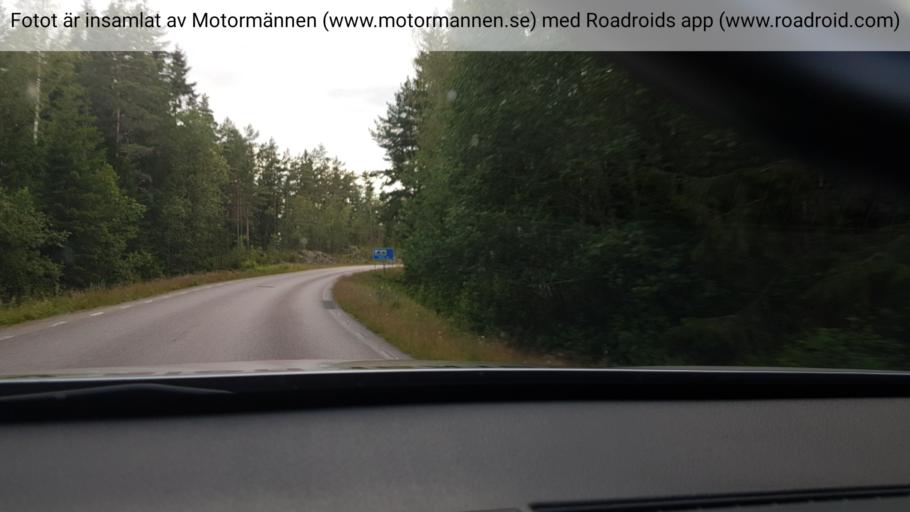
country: SE
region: Vaermland
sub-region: Forshaga Kommun
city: Deje
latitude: 59.7426
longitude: 13.3667
